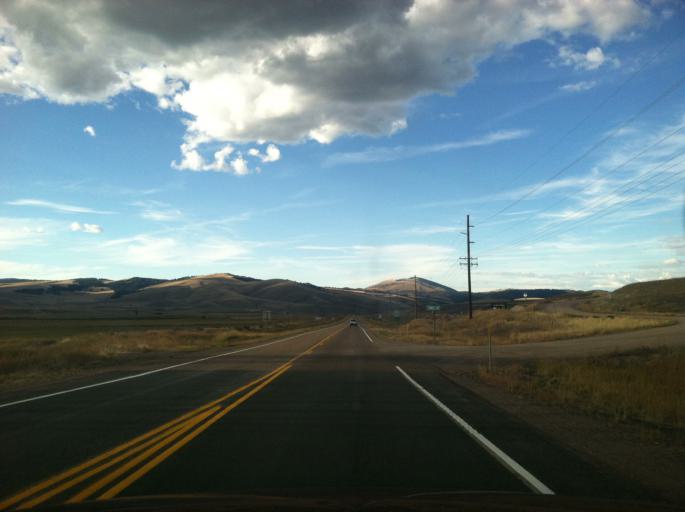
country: US
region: Montana
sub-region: Granite County
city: Philipsburg
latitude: 46.3398
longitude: -113.3117
